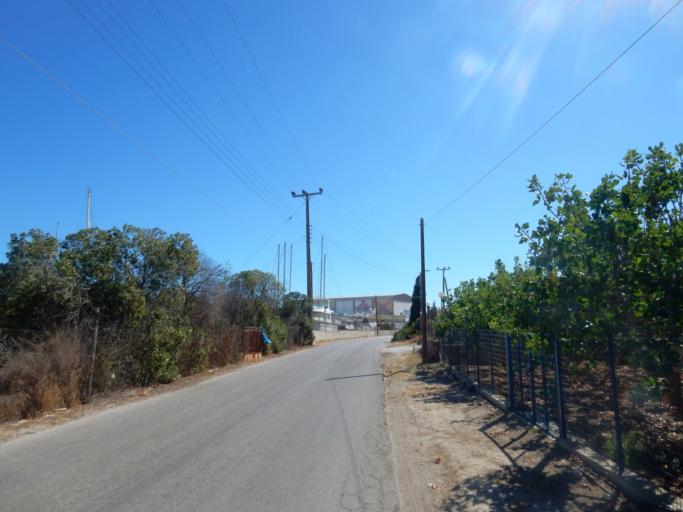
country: GR
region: Attica
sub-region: Nomos Piraios
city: Kypseli
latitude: 37.7699
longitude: 23.4557
